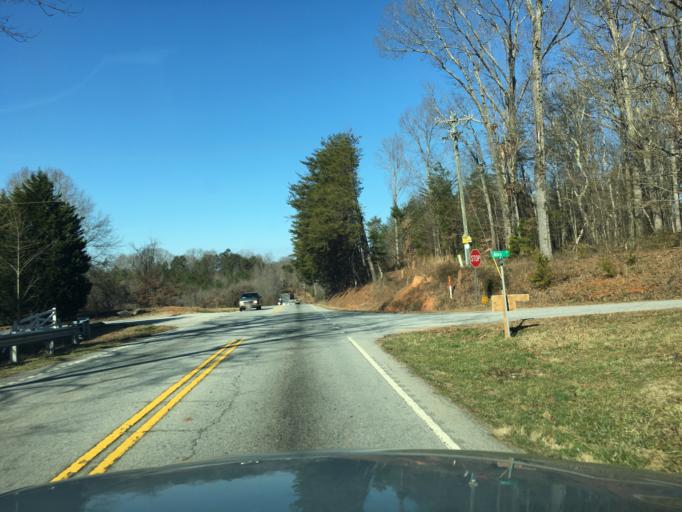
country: US
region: South Carolina
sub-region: Greenville County
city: Berea
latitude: 34.8884
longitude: -82.5256
